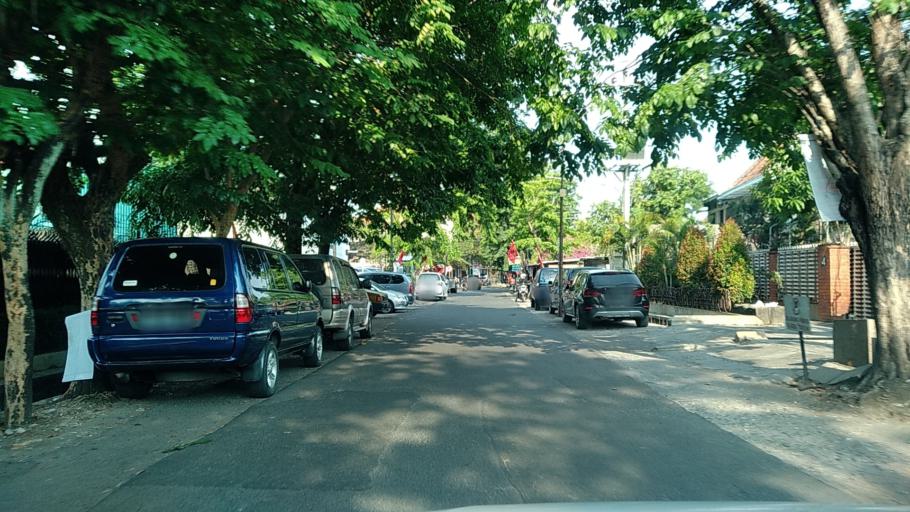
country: ID
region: Central Java
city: Semarang
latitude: -6.9962
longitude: 110.4311
